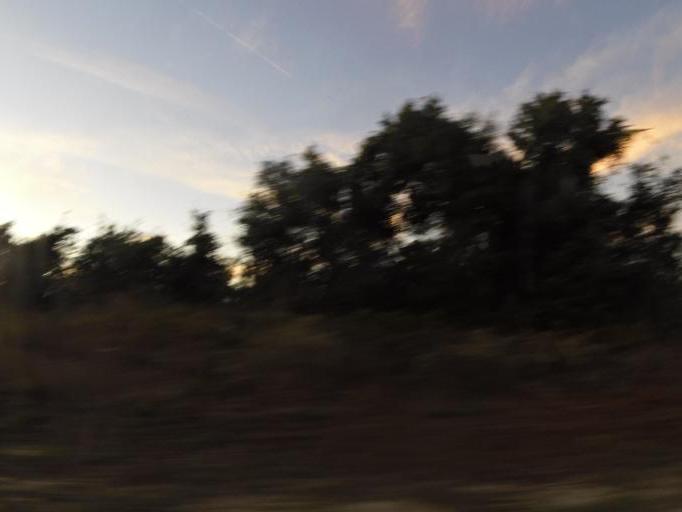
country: US
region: Florida
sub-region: Duval County
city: Jacksonville
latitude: 30.4128
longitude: -81.6220
